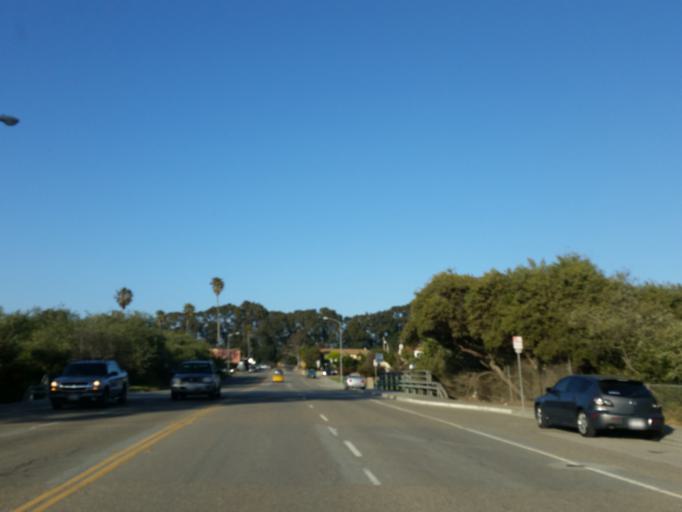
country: US
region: California
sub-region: San Luis Obispo County
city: Oceano
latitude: 35.1064
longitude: -120.6266
